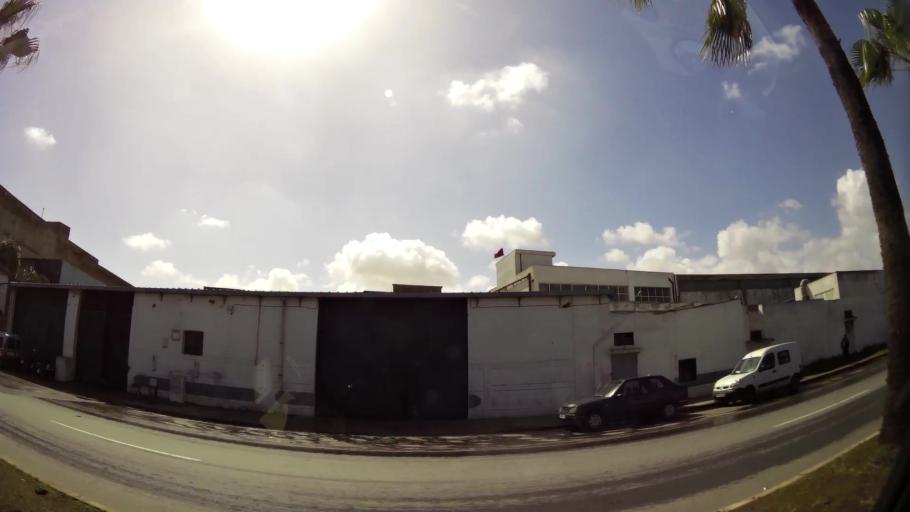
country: MA
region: Grand Casablanca
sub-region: Mediouna
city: Tit Mellil
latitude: 33.6180
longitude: -7.5165
